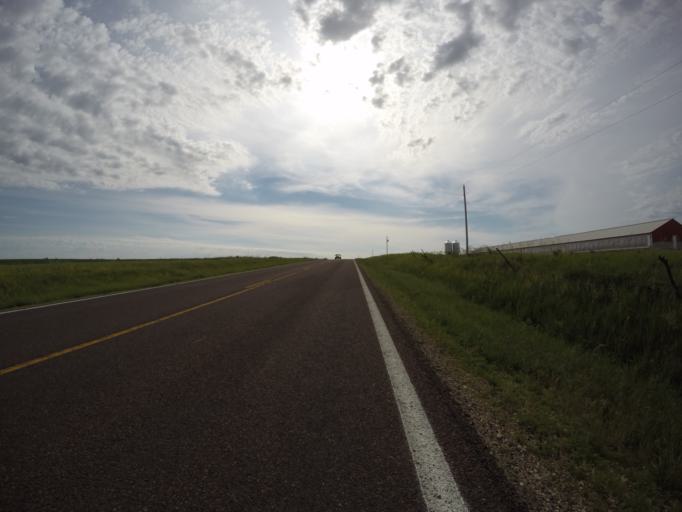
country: US
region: Kansas
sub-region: Washington County
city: Washington
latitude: 39.7122
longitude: -97.3400
